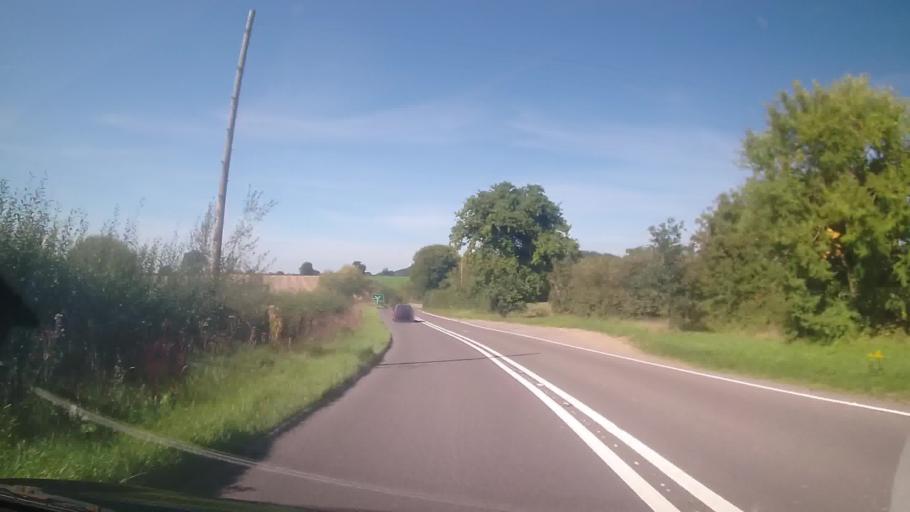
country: GB
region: England
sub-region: Shropshire
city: Lydham
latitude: 52.5185
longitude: -2.9830
